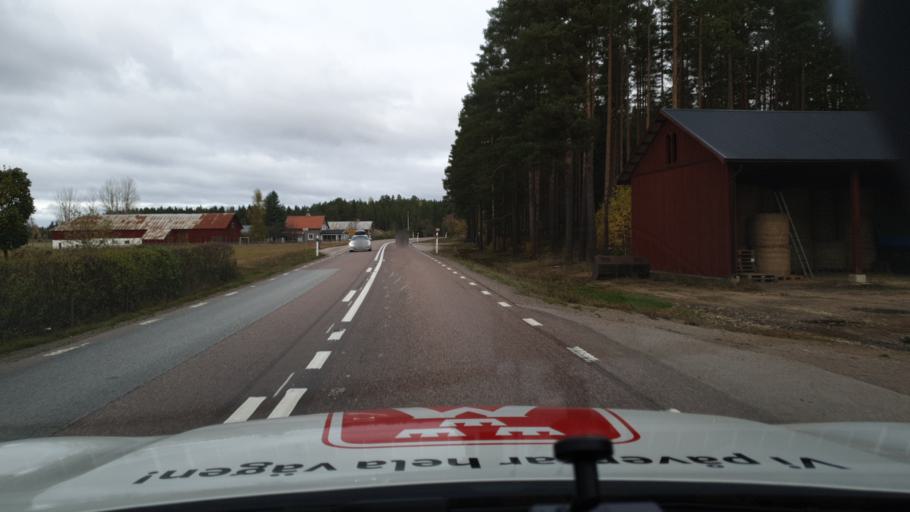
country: SE
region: Gaevleborg
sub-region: Gavle Kommun
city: Hedesunda
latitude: 60.4354
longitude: 16.9674
